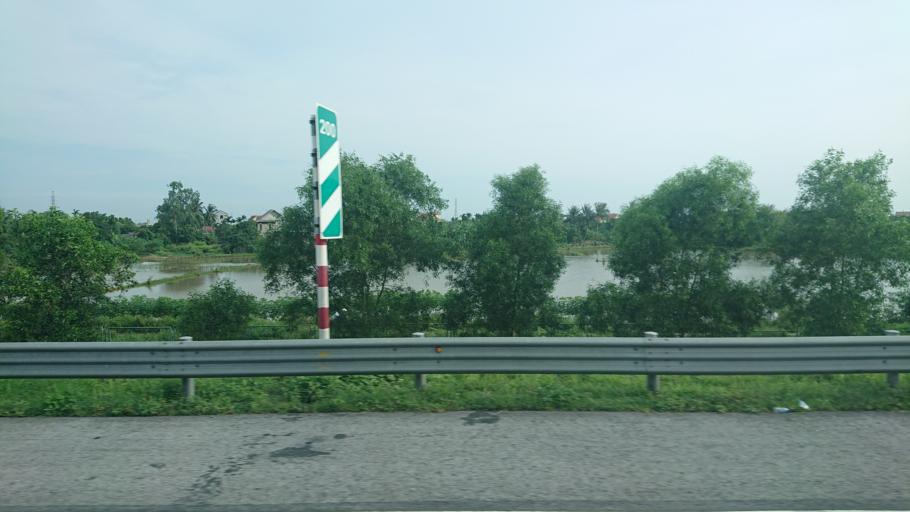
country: VN
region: Hai Phong
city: An Lao
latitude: 20.8052
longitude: 106.5196
